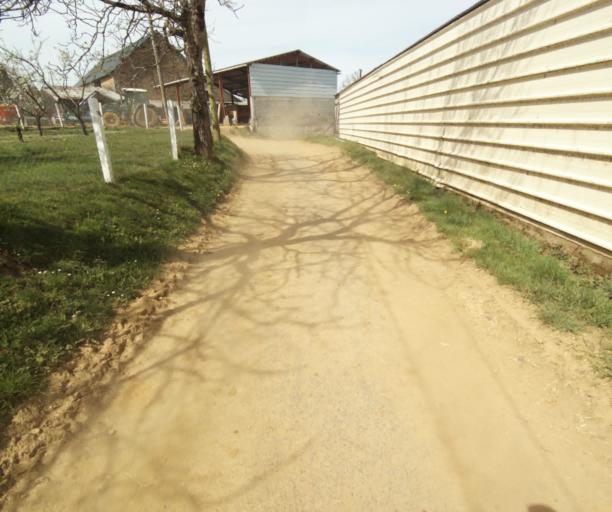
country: FR
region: Limousin
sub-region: Departement de la Correze
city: Correze
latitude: 45.3820
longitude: 1.8108
